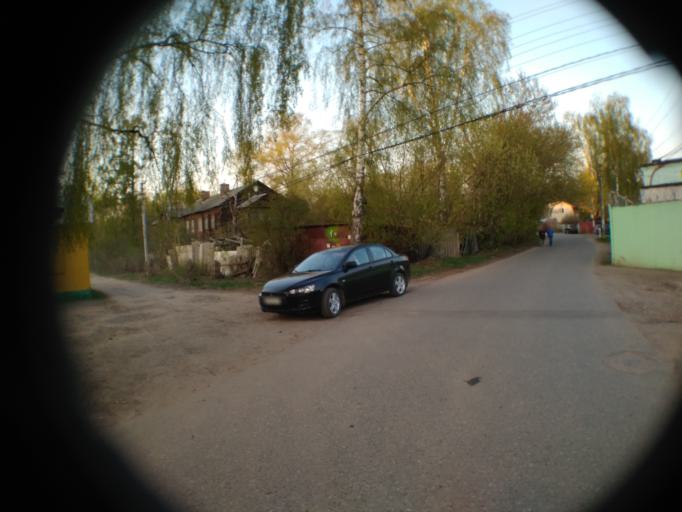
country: RU
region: Moskovskaya
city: Zhukovskiy
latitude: 55.5876
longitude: 38.1422
